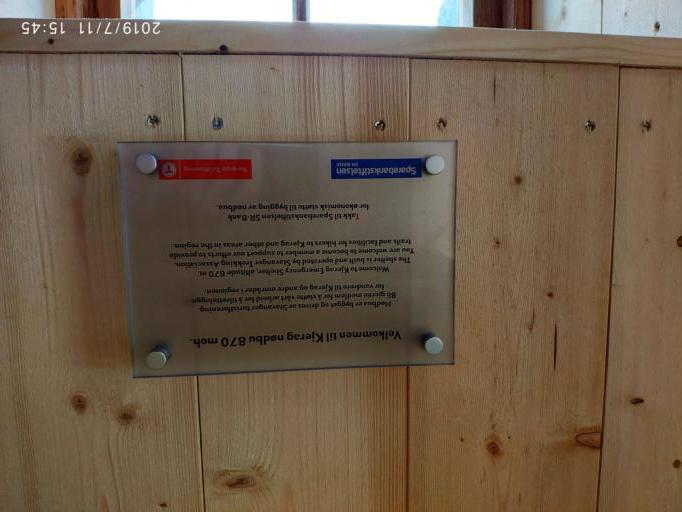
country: NO
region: Vest-Agder
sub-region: Sirdal
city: Tonstad
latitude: 59.0413
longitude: 6.6312
